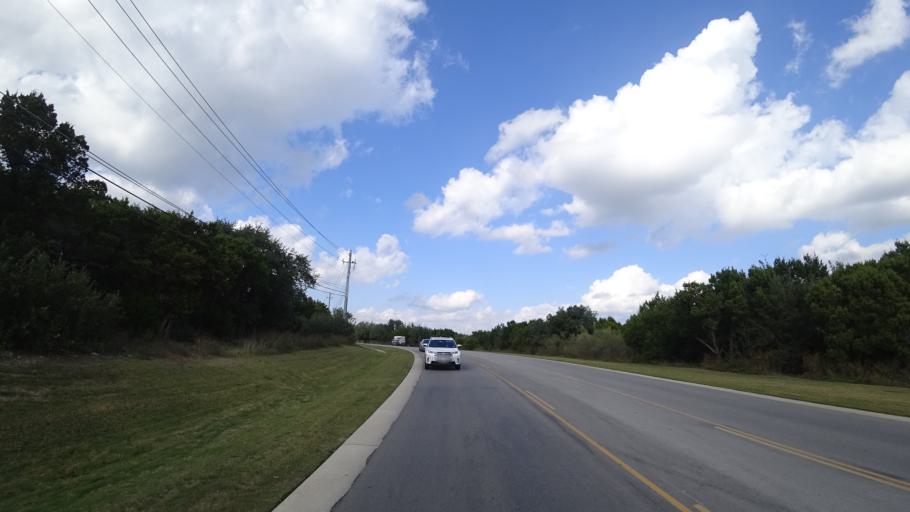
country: US
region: Texas
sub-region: Travis County
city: Barton Creek
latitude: 30.2758
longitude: -97.8842
